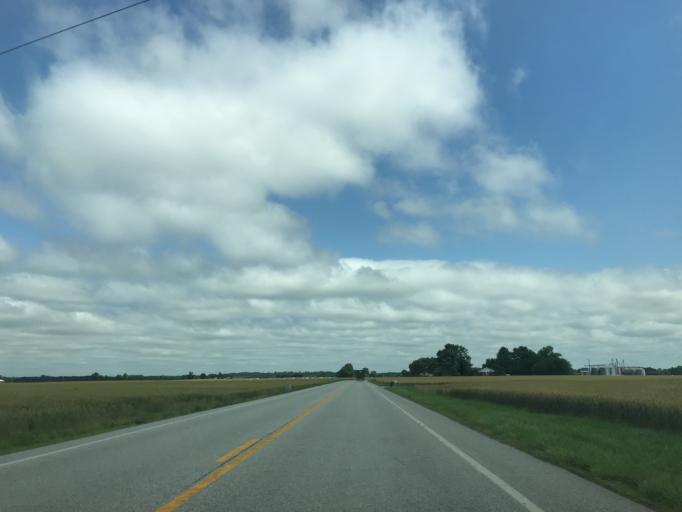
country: US
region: Maryland
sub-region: Caroline County
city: Ridgely
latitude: 38.9255
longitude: -75.8935
